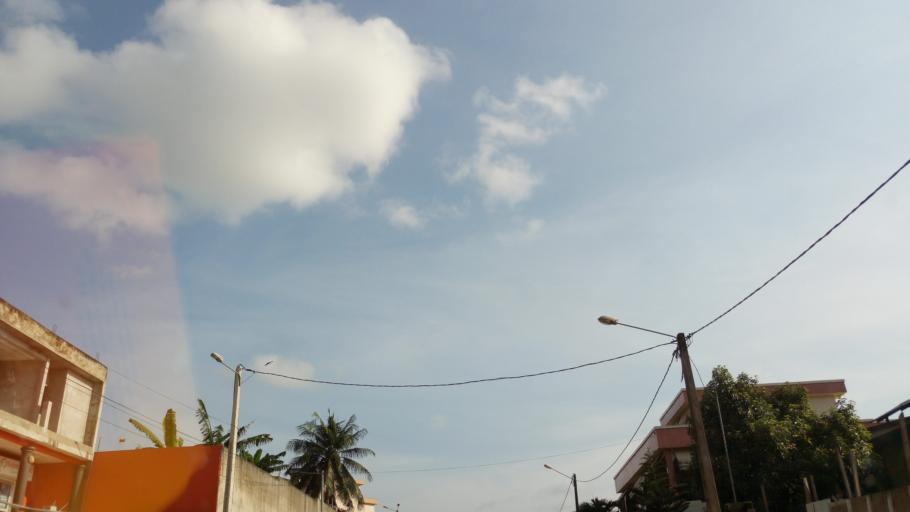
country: CI
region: Lagunes
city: Bingerville
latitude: 5.3779
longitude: -3.9510
